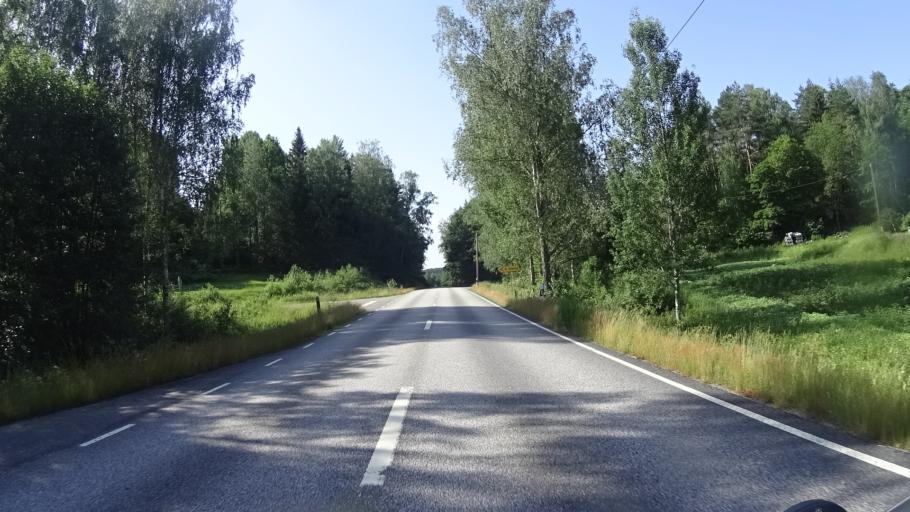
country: SE
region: Kalmar
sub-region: Vasterviks Kommun
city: Overum
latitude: 58.0270
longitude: 16.2384
